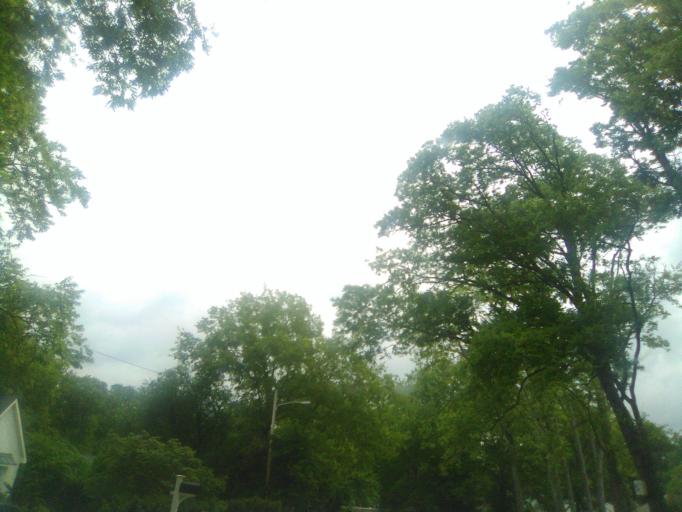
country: US
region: Tennessee
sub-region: Davidson County
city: Belle Meade
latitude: 36.1038
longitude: -86.8755
